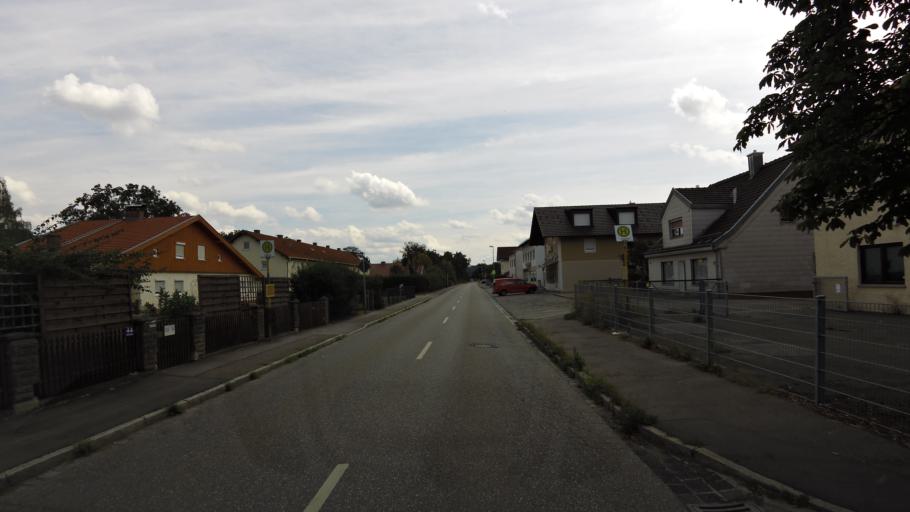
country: DE
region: Bavaria
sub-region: Upper Bavaria
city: Unterneukirchen
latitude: 48.1490
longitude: 12.6171
